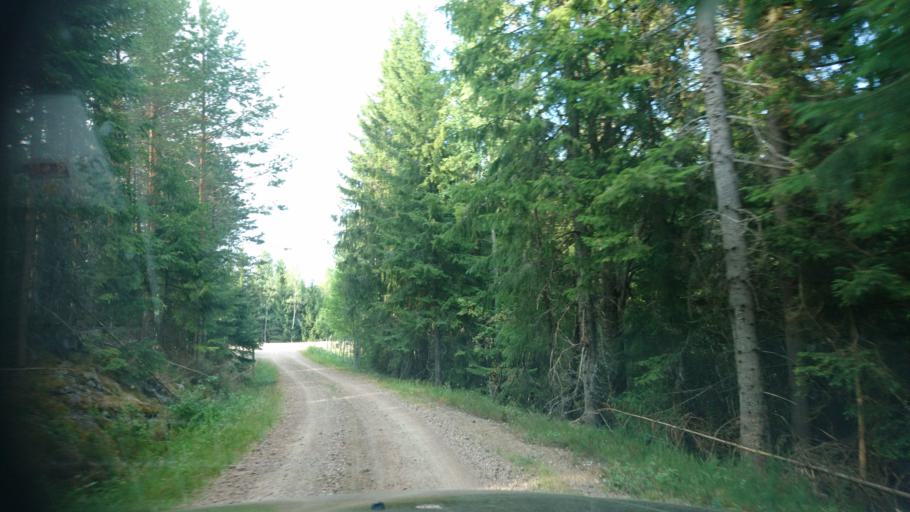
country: SE
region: Vaermland
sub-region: Kristinehamns Kommun
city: Bjorneborg
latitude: 59.3108
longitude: 14.3136
